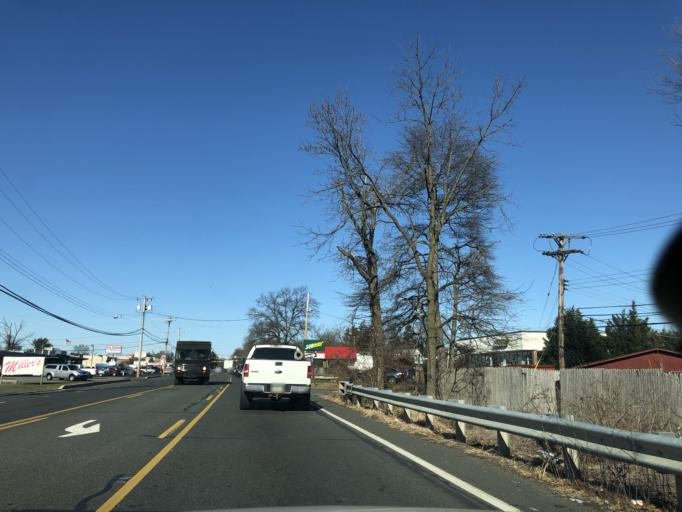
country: US
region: Pennsylvania
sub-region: Bucks County
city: Hulmeville
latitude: 40.1314
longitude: -74.8834
